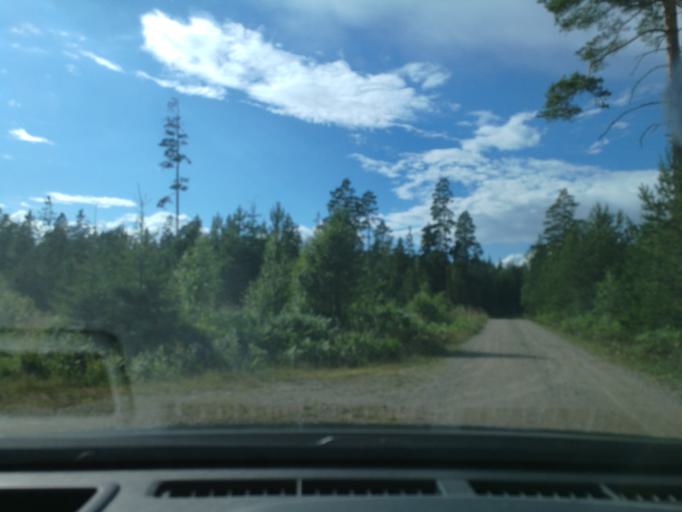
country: SE
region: Vaestmanland
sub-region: Surahammars Kommun
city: Ramnas
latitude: 59.8321
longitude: 16.2437
